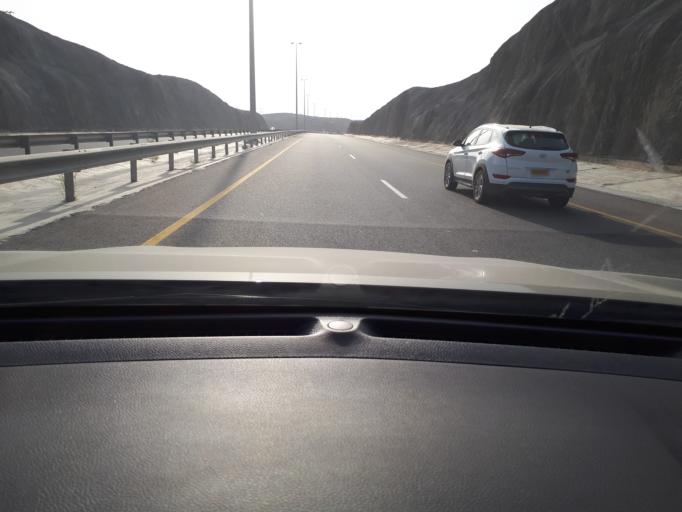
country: OM
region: Muhafazat Masqat
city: Muscat
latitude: 23.1912
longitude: 58.8462
